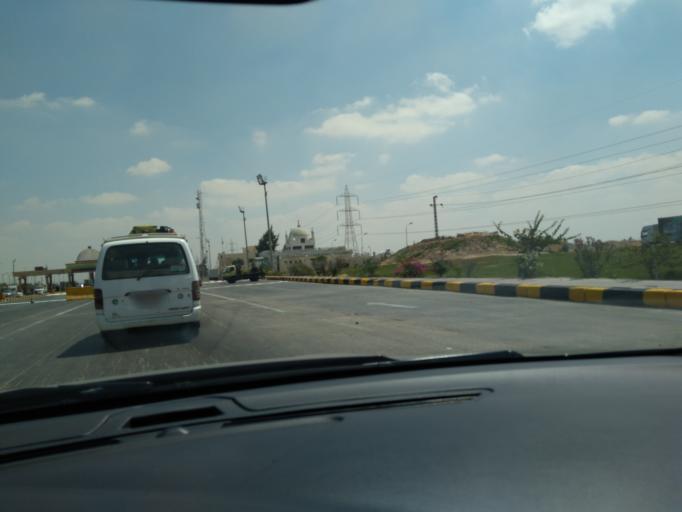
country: EG
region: Al Isma'iliyah
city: At Tall al Kabir
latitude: 30.4052
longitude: 31.9955
